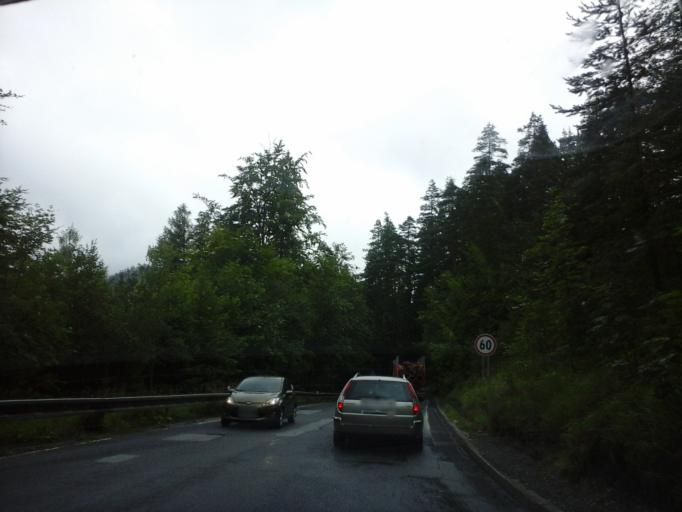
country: SK
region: Kosicky
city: Dobsina
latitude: 48.9075
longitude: 20.2571
